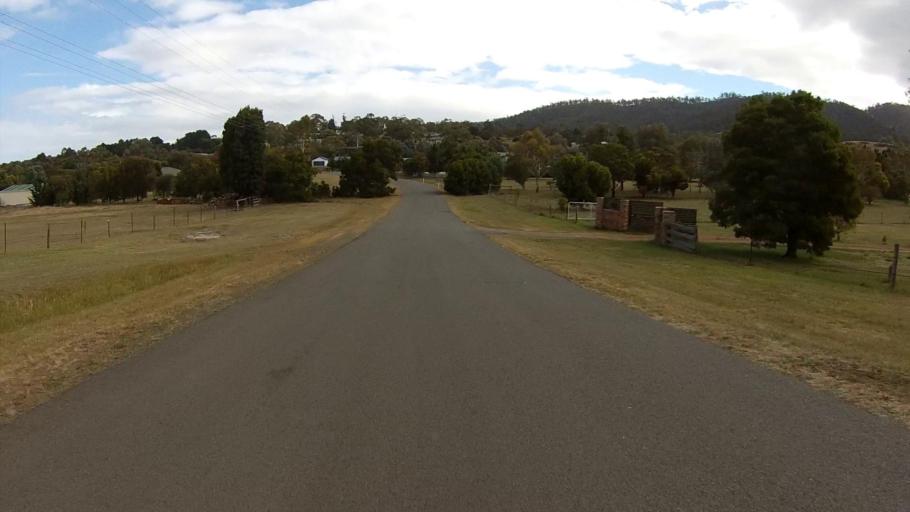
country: AU
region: Tasmania
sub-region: Clarence
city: Seven Mile Beach
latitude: -42.8562
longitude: 147.4836
